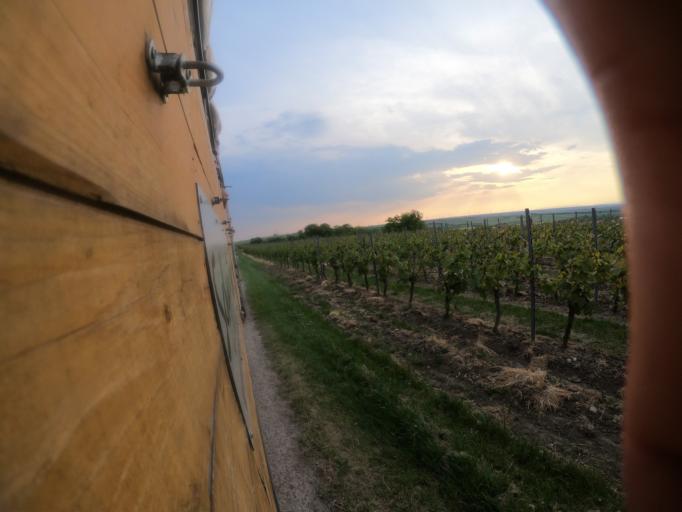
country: DE
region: Rheinland-Pfalz
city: Dalheim
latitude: 49.8243
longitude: 8.3010
